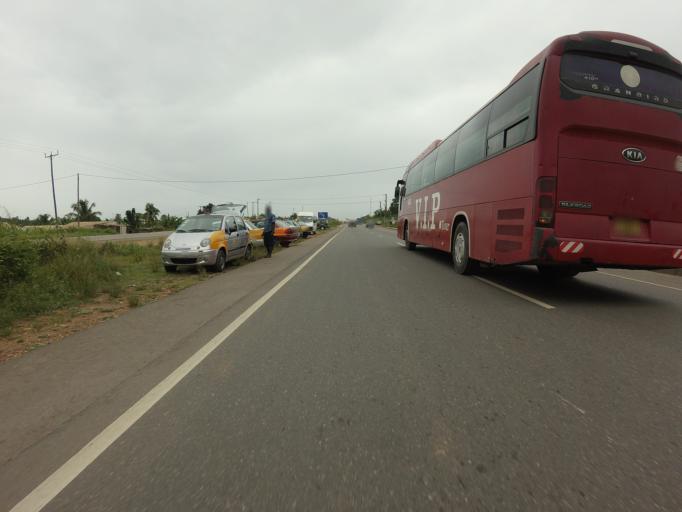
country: GH
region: Eastern
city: Suhum
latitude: 6.0409
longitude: -0.4577
